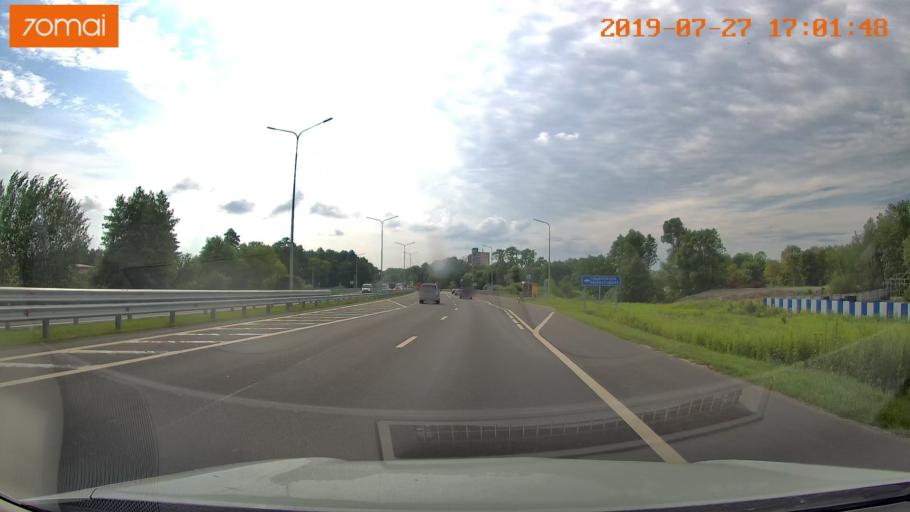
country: RU
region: Kaliningrad
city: Bol'shoe Isakovo
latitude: 54.7074
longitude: 20.6250
